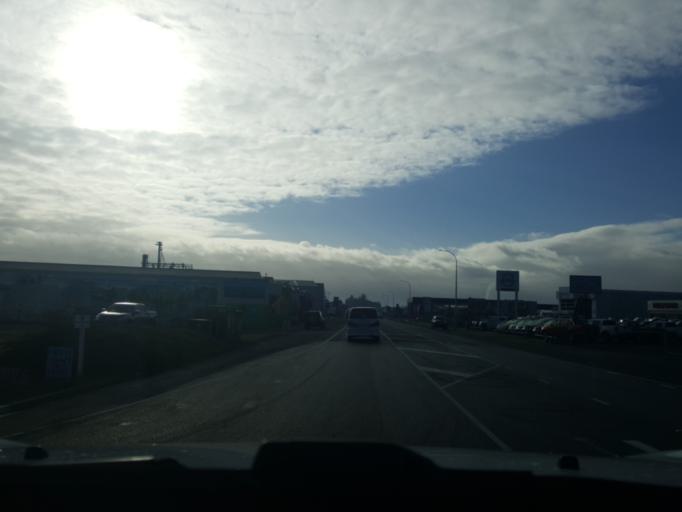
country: NZ
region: Waikato
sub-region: Waipa District
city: Cambridge
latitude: -37.6617
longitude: 175.5175
